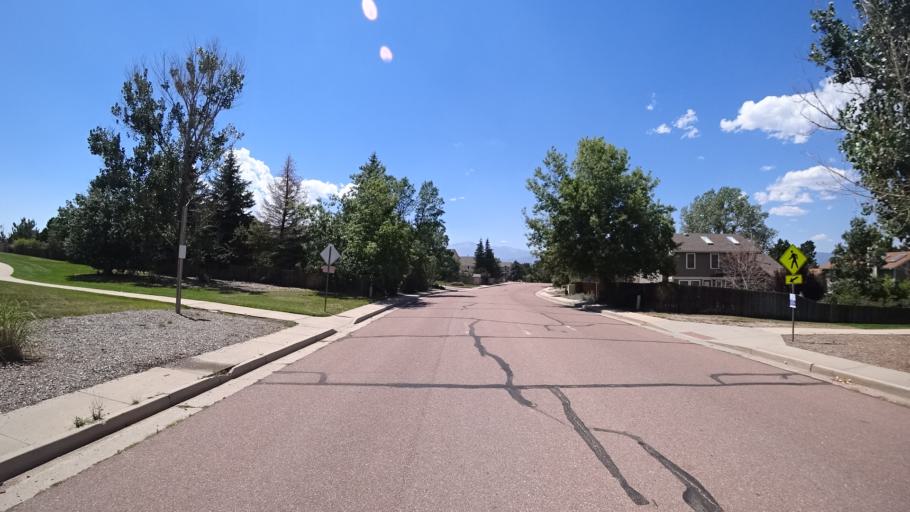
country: US
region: Colorado
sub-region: El Paso County
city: Black Forest
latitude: 38.9490
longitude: -104.7481
